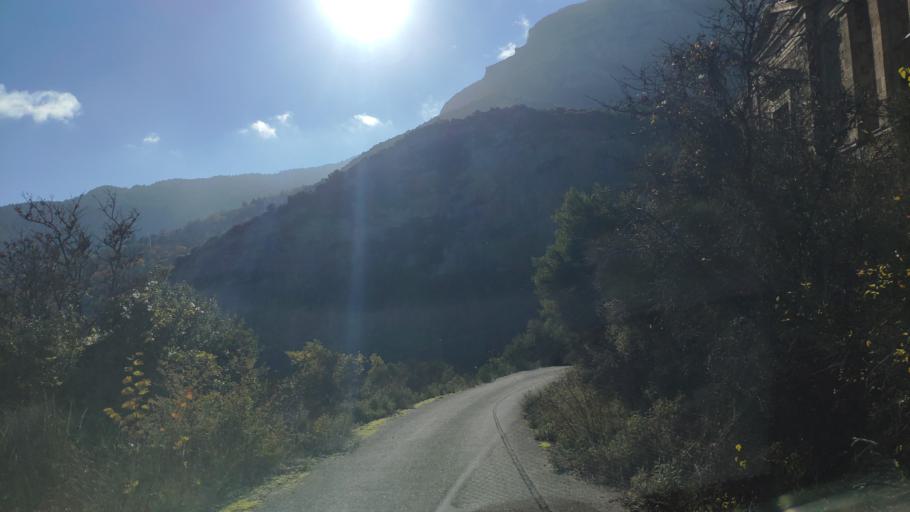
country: GR
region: West Greece
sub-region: Nomos Achaias
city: Aiyira
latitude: 38.0508
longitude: 22.4496
